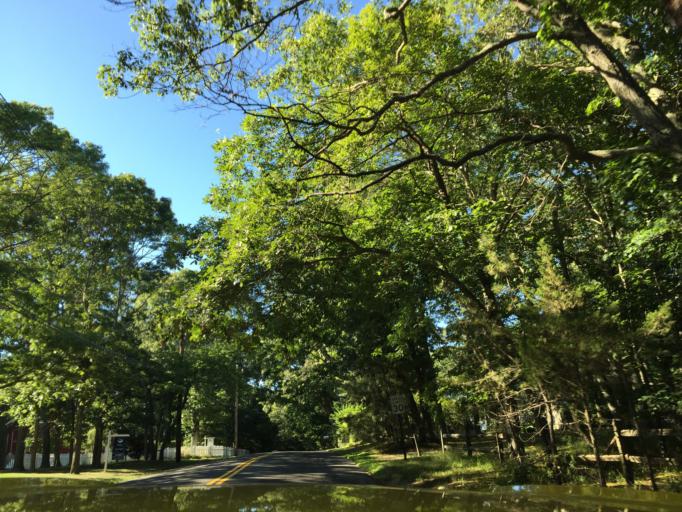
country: US
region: New York
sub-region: Suffolk County
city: Southold
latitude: 41.0435
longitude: -72.4102
